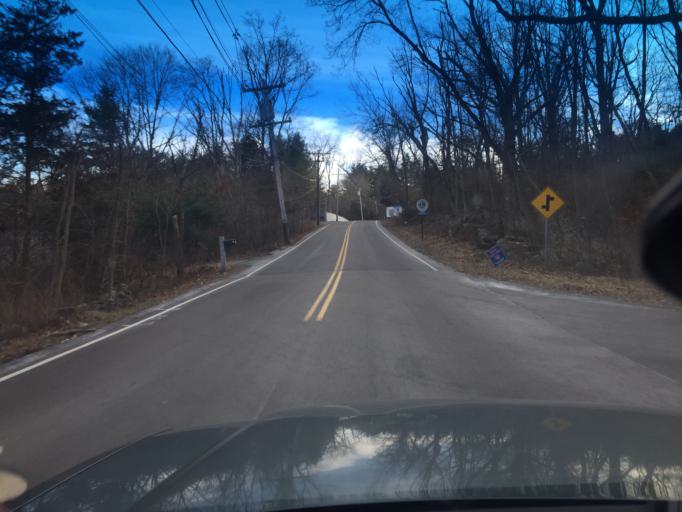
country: US
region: Massachusetts
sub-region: Middlesex County
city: Holliston
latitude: 42.1786
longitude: -71.4114
